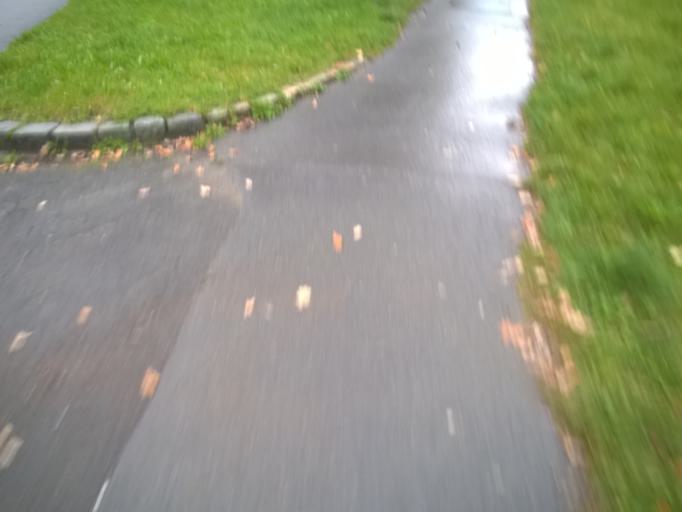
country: CZ
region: Praha
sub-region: Praha 9
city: Vysocany
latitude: 50.0942
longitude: 14.5087
